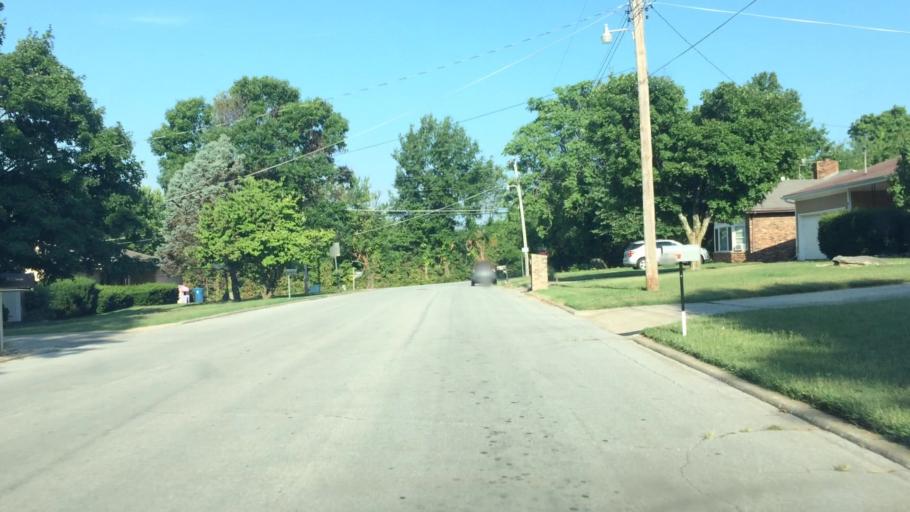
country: US
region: Missouri
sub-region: Greene County
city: Springfield
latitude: 37.2594
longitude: -93.2800
